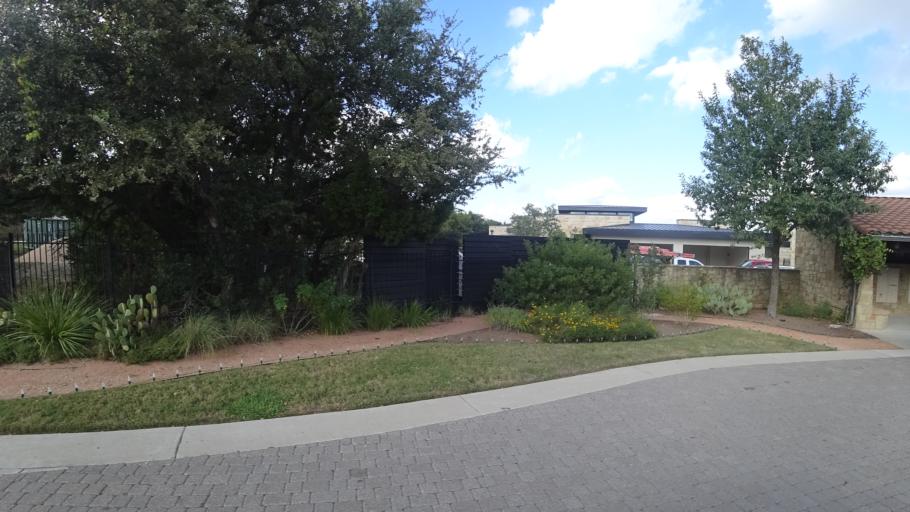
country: US
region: Texas
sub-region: Travis County
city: Barton Creek
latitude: 30.2808
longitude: -97.8839
